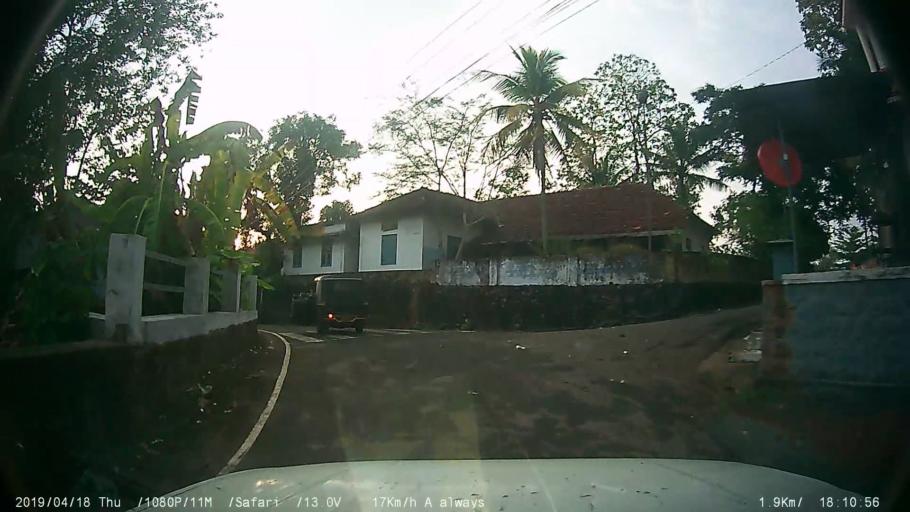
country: IN
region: Kerala
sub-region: Kottayam
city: Palackattumala
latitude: 9.7800
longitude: 76.5776
